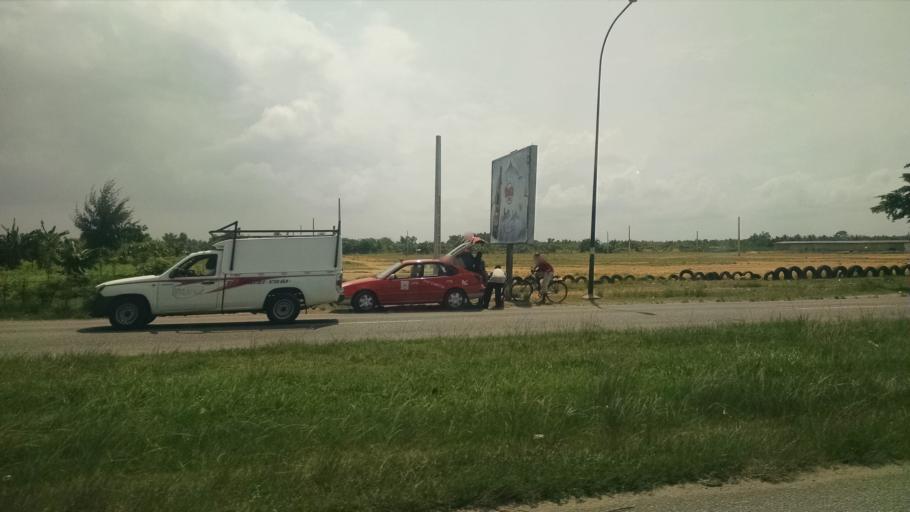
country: CI
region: Lagunes
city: Abidjan
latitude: 5.2633
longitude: -3.9499
